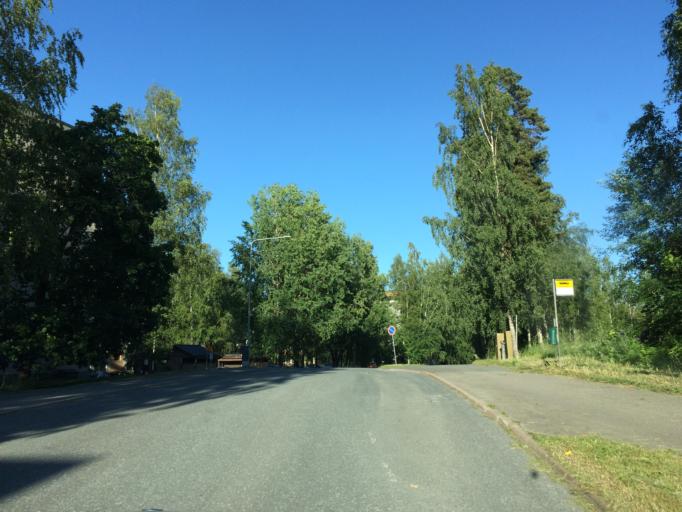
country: FI
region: Haeme
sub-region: Haemeenlinna
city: Haemeenlinna
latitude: 60.9864
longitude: 24.5132
